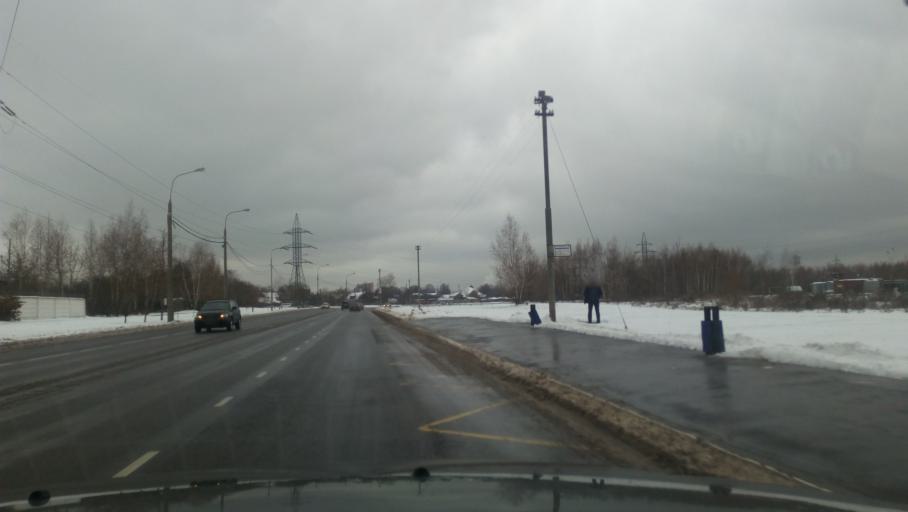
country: RU
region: Moscow
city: Zhulebino
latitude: 55.7211
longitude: 37.8662
